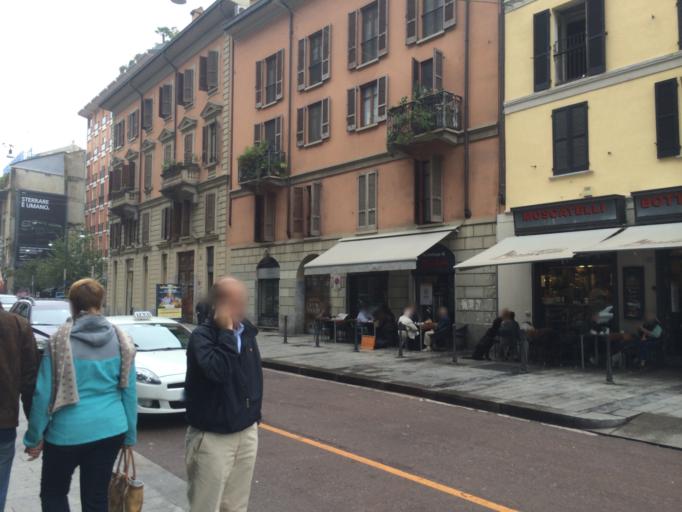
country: IT
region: Lombardy
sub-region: Citta metropolitana di Milano
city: Milano
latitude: 45.4769
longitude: 9.1847
